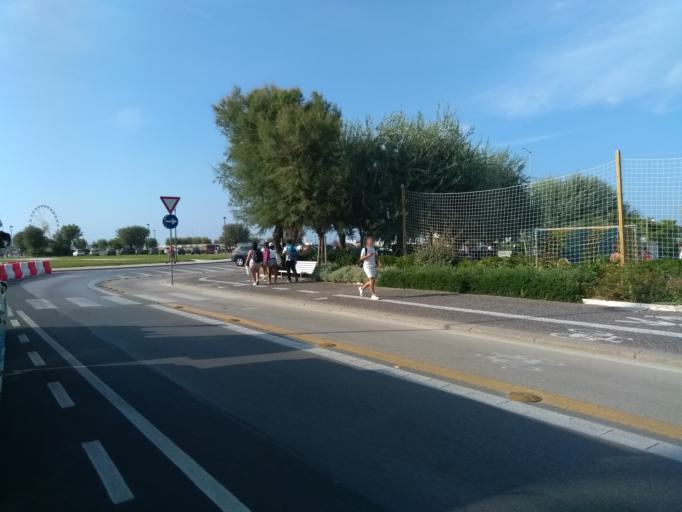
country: IT
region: Emilia-Romagna
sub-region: Provincia di Rimini
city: Rimini
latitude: 44.0721
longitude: 12.5785
